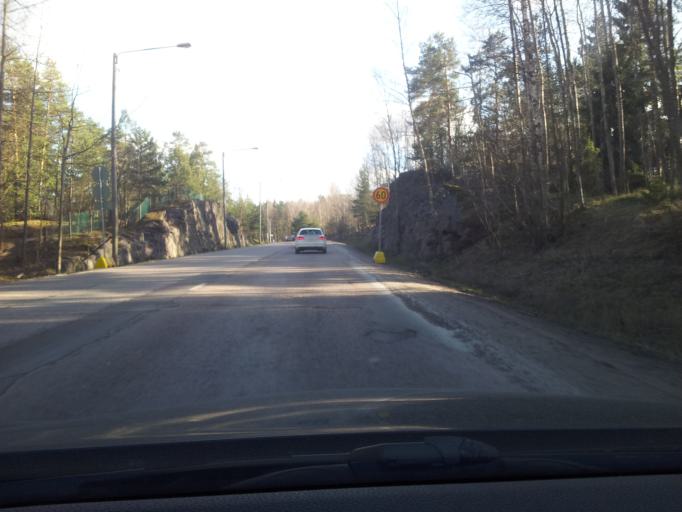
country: FI
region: Uusimaa
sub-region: Helsinki
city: Espoo
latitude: 60.1401
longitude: 24.6774
